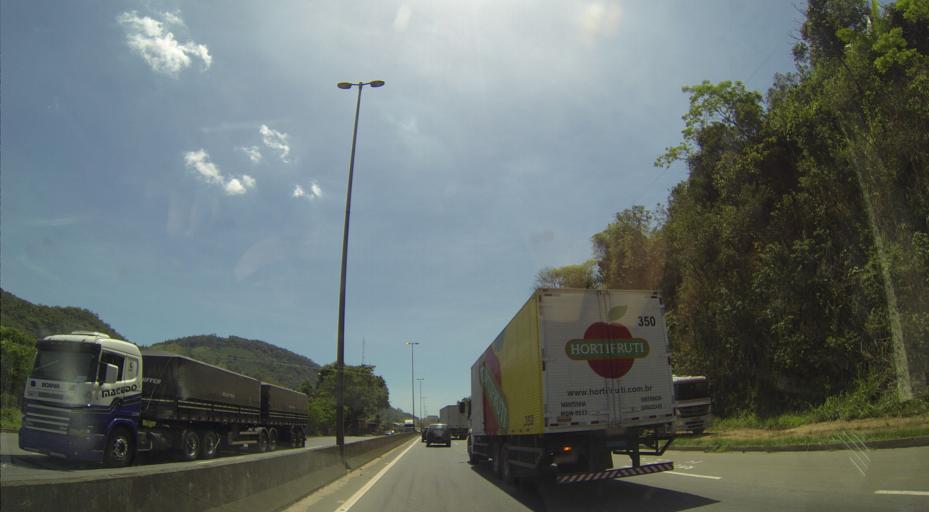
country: BR
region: Espirito Santo
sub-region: Viana
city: Viana
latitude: -20.3835
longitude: -40.4606
